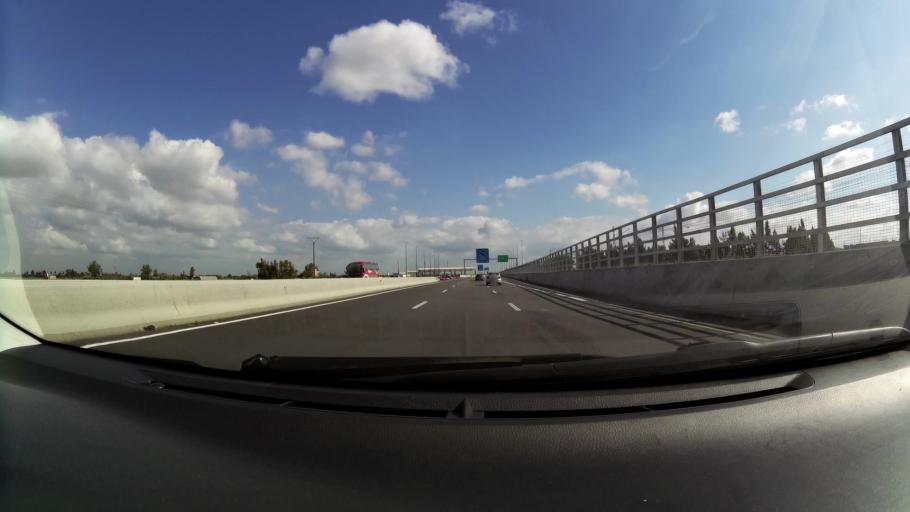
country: MA
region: Chaouia-Ouardigha
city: Nouaseur
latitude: 33.3254
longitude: -7.6066
